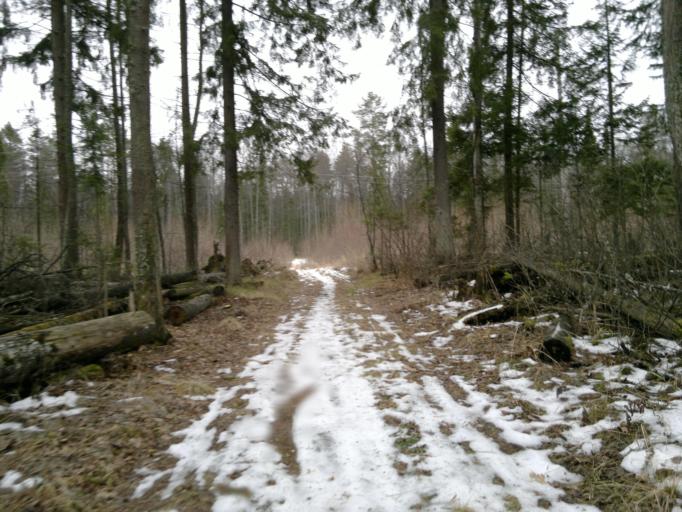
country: RU
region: Mariy-El
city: Yoshkar-Ola
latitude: 56.6073
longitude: 47.9607
